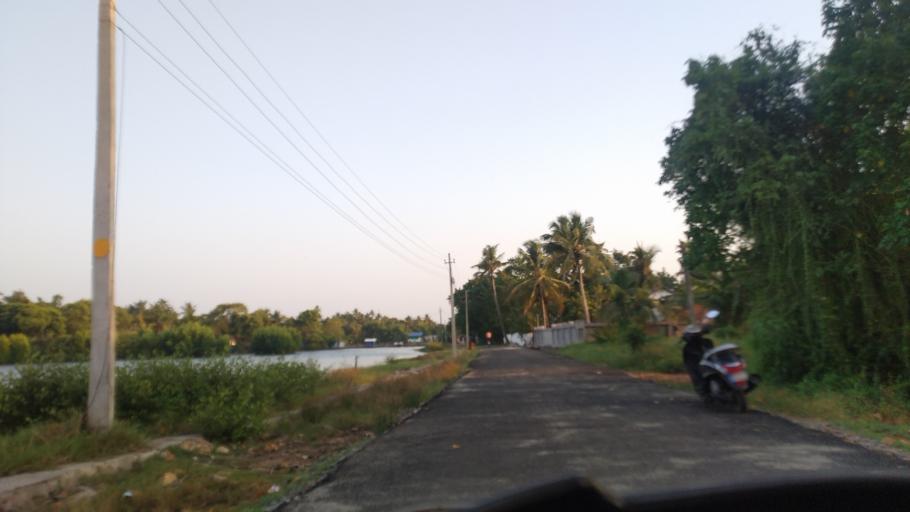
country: IN
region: Kerala
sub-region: Ernakulam
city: Elur
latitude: 10.0511
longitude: 76.2266
